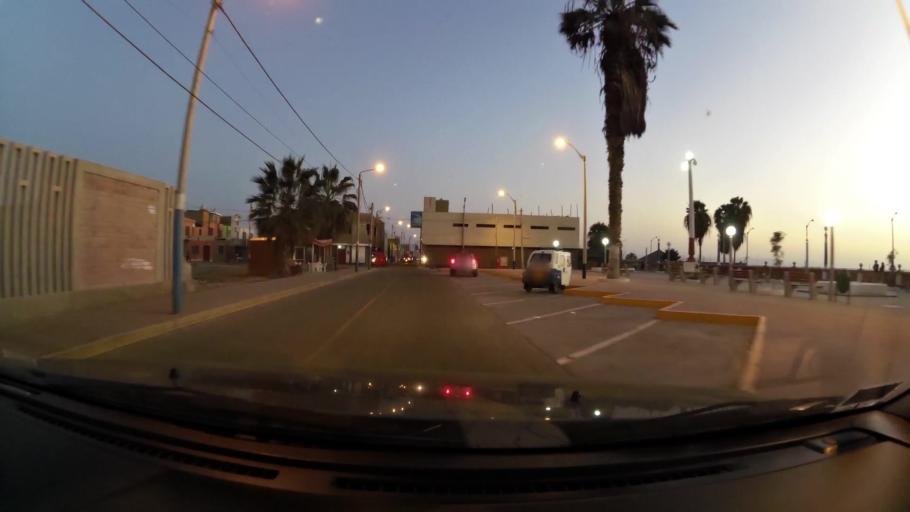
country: PE
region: Ica
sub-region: Provincia de Pisco
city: Pisco
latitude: -13.7111
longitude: -76.2184
